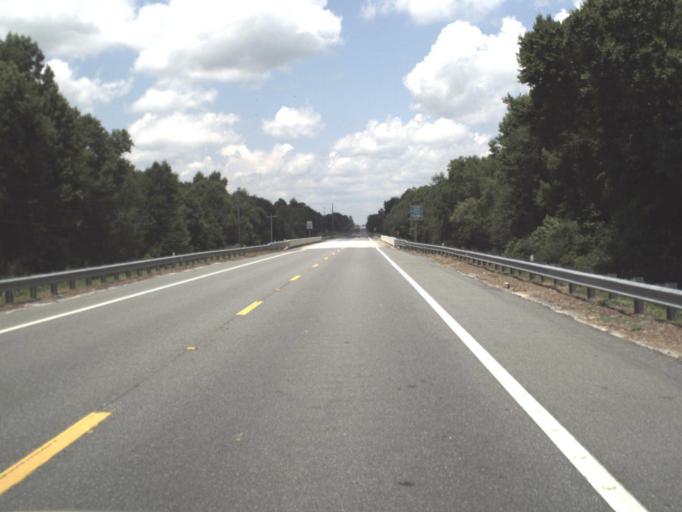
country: US
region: Florida
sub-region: Alachua County
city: High Springs
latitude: 30.0042
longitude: -82.5710
